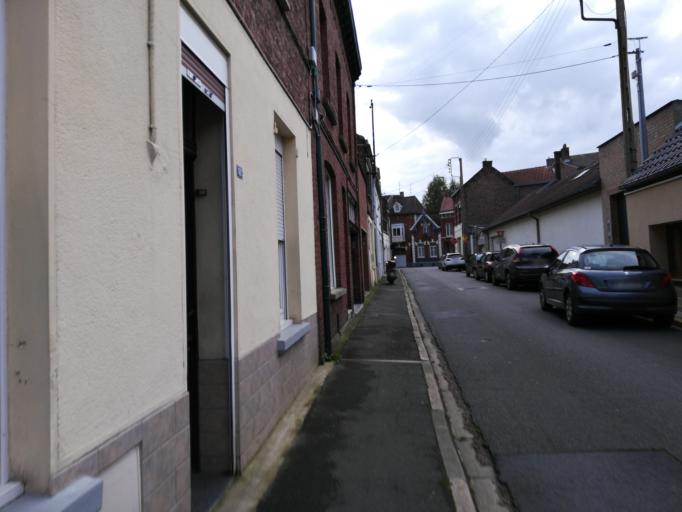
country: FR
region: Nord-Pas-de-Calais
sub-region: Departement du Pas-de-Calais
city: Montigny-en-Gohelle
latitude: 50.4245
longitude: 2.9454
